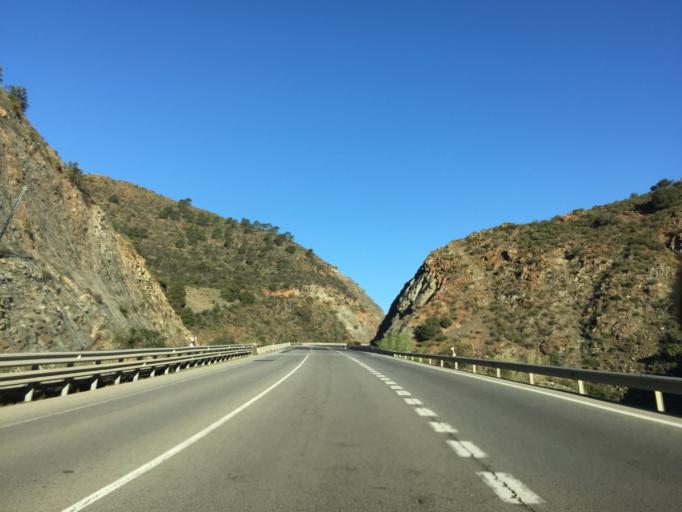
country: ES
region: Andalusia
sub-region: Provincia de Malaga
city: Carratraca
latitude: 36.8240
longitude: -4.7972
